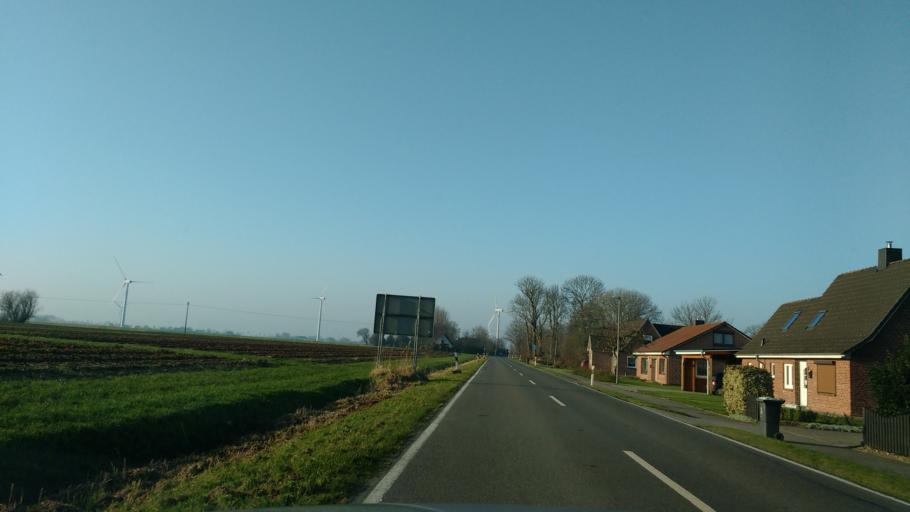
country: DE
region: Schleswig-Holstein
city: Trennewurth
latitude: 54.0005
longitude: 9.0220
